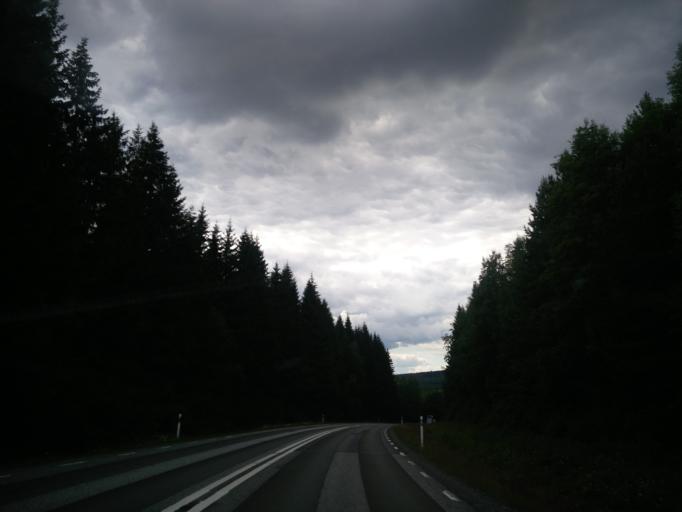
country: SE
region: Vaermland
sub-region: Filipstads Kommun
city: Filipstad
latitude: 59.7855
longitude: 14.3299
